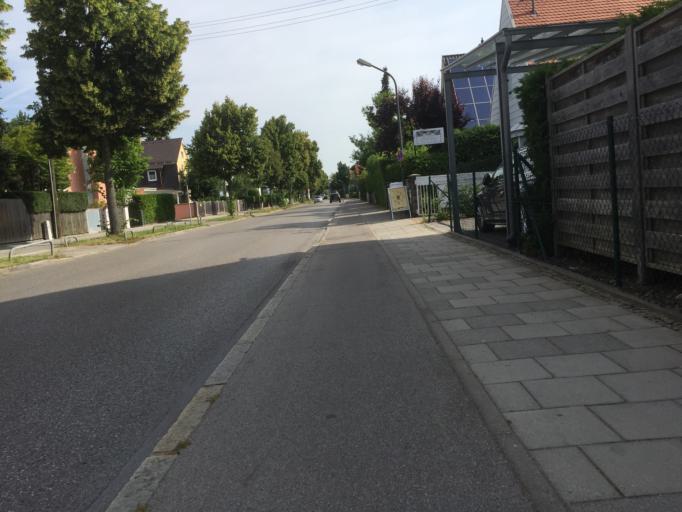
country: DE
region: Bavaria
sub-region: Upper Bavaria
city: Bogenhausen
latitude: 48.1186
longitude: 11.6409
